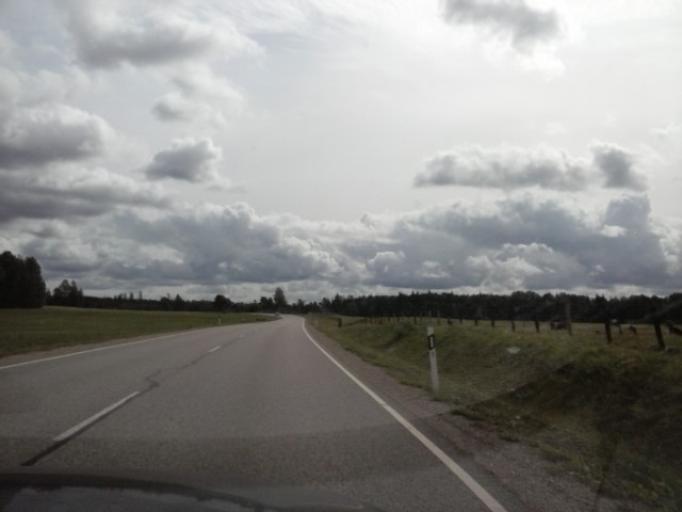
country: LV
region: Kuldigas Rajons
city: Kuldiga
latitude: 56.9610
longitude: 22.0897
